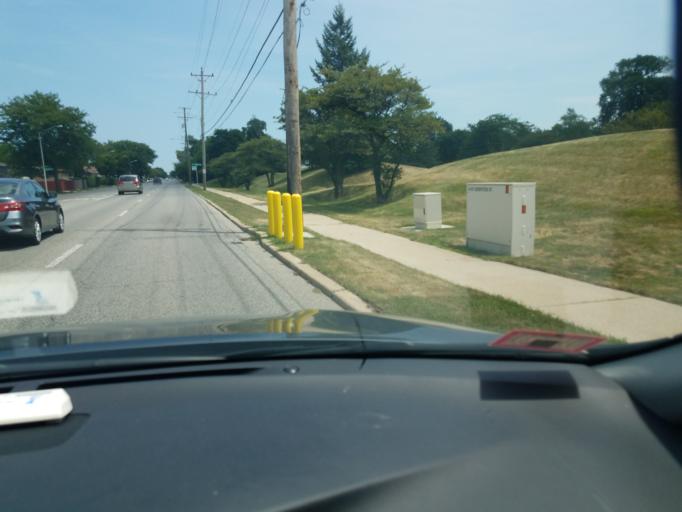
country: US
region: Illinois
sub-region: Cook County
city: Skokie
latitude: 42.0407
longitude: -87.7391
